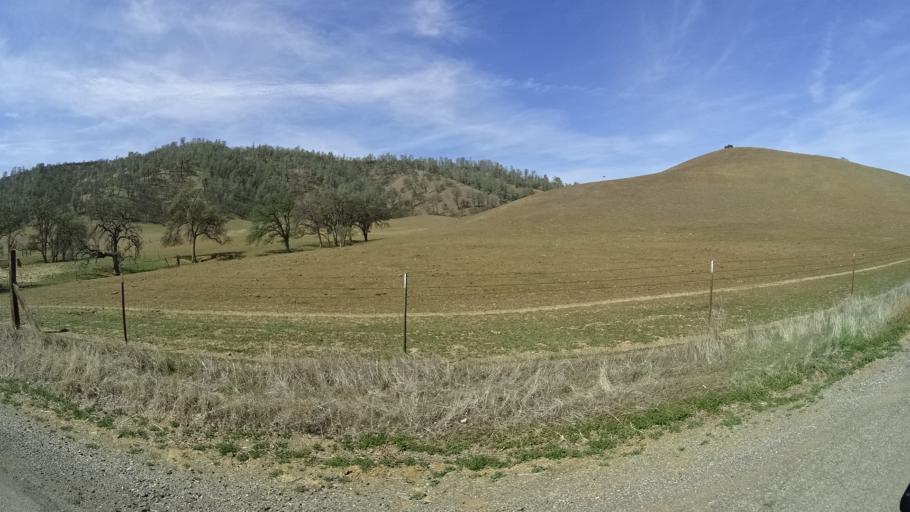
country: US
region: California
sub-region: Glenn County
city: Willows
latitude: 39.4834
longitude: -122.4536
